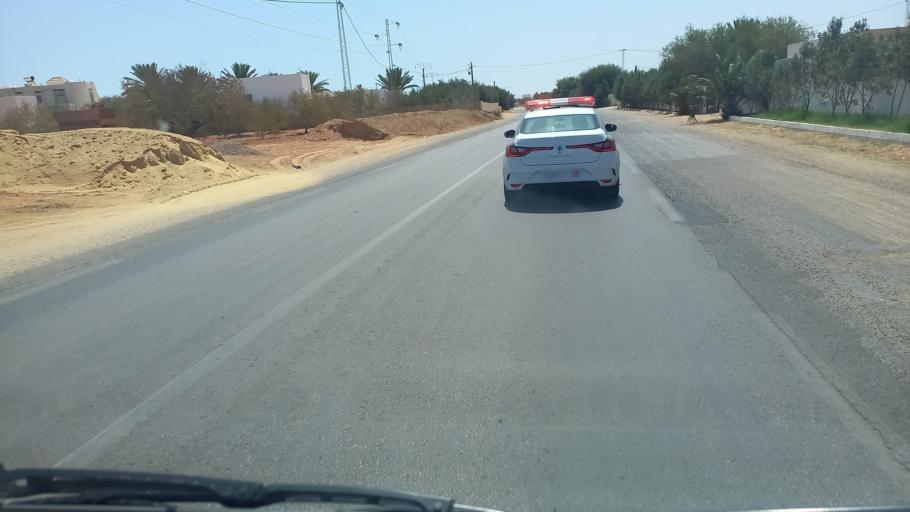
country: TN
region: Madanin
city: Midoun
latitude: 33.7662
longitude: 10.9037
